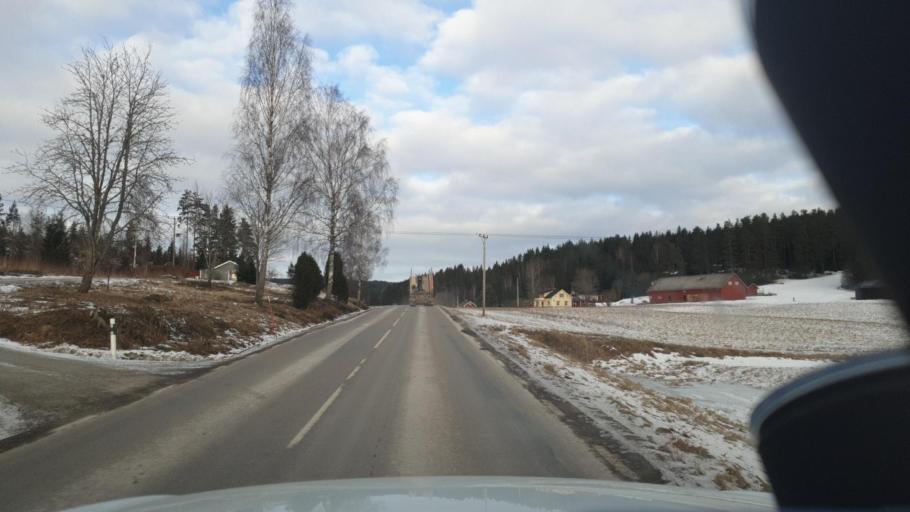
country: SE
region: Vaermland
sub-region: Arvika Kommun
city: Arvika
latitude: 59.7294
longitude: 12.6425
